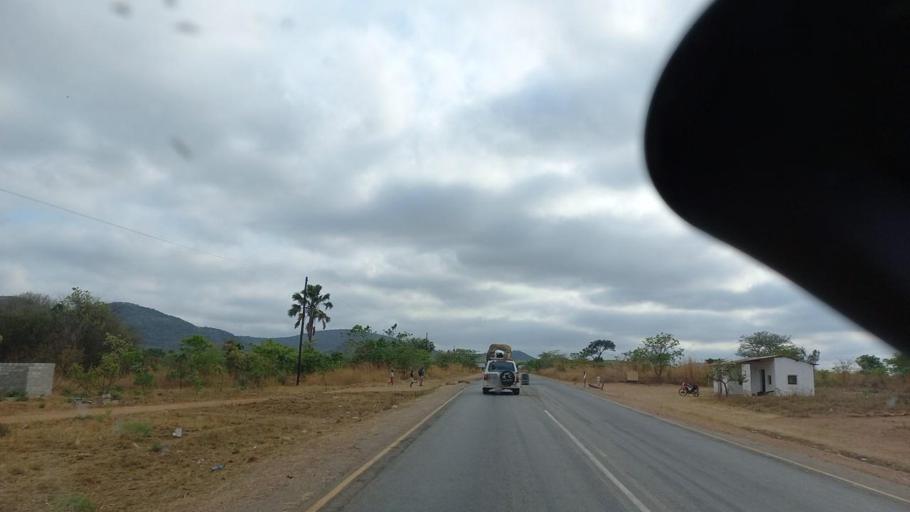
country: ZM
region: Lusaka
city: Chongwe
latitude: -15.2402
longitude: 29.1644
